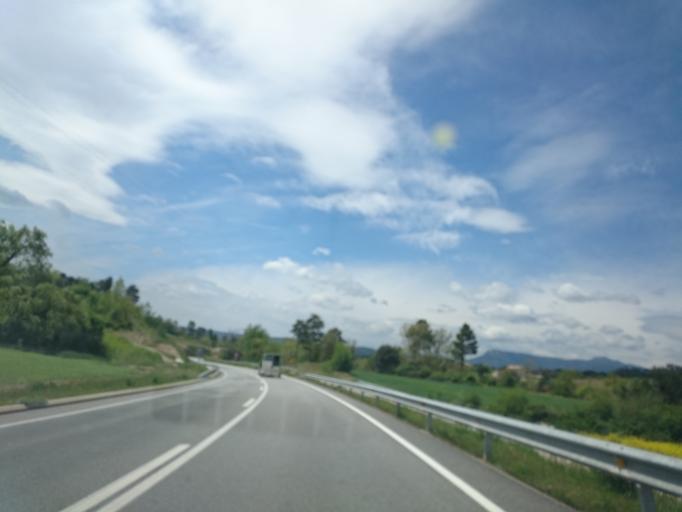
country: ES
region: Catalonia
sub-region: Provincia de Barcelona
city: Olvan
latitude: 42.0519
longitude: 1.9118
